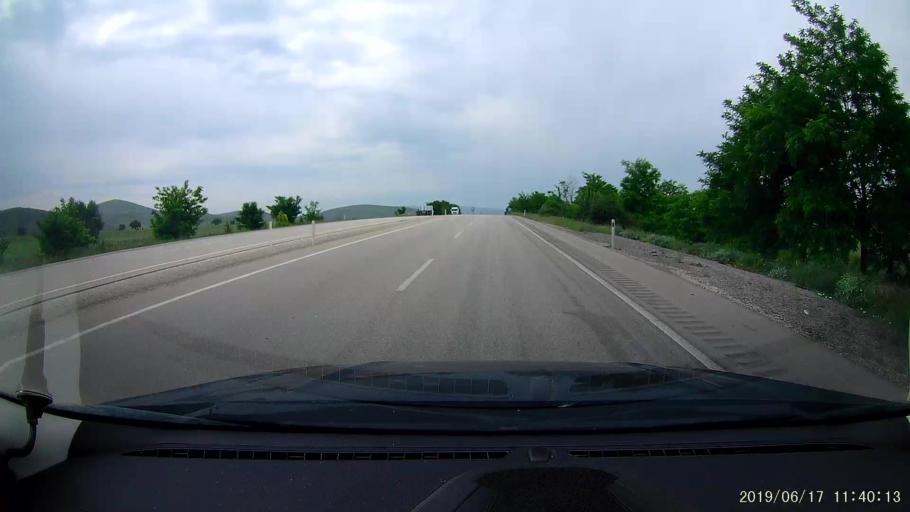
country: TR
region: Cankiri
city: Kursunlu
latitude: 40.8357
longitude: 33.3559
